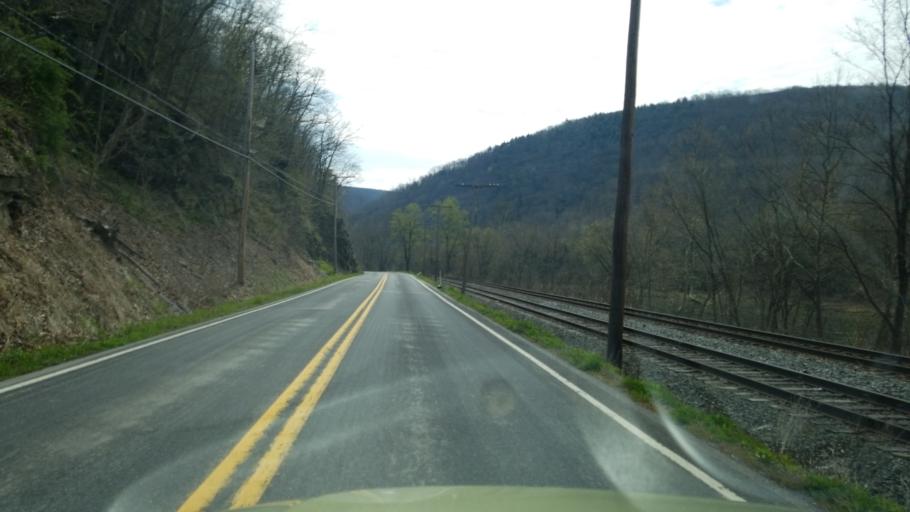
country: US
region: Pennsylvania
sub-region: Clinton County
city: Renovo
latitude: 41.2796
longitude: -77.8733
